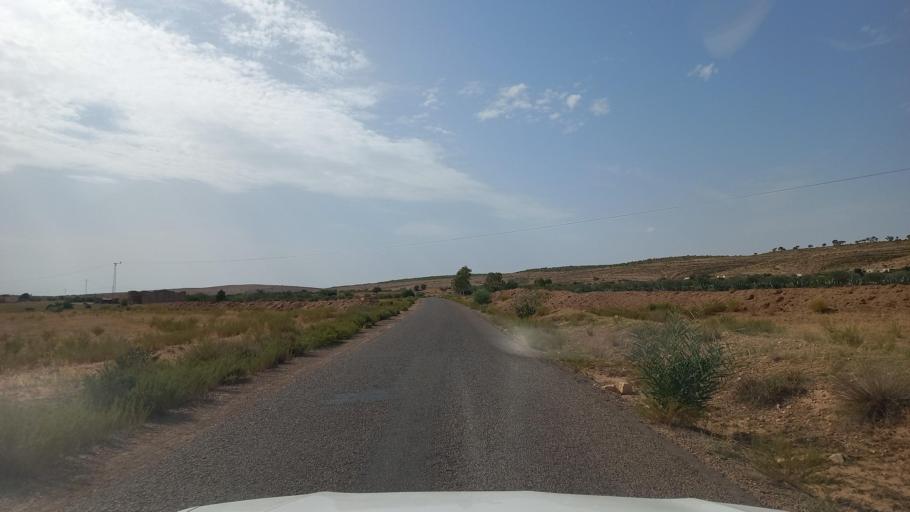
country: TN
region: Al Qasrayn
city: Kasserine
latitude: 35.3666
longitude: 8.8716
